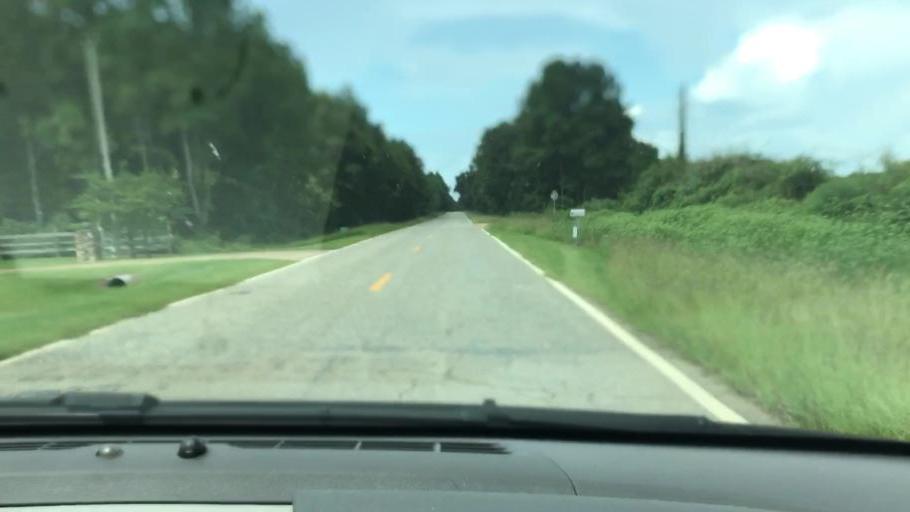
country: US
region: Georgia
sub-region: Seminole County
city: Donalsonville
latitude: 31.1461
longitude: -84.9948
